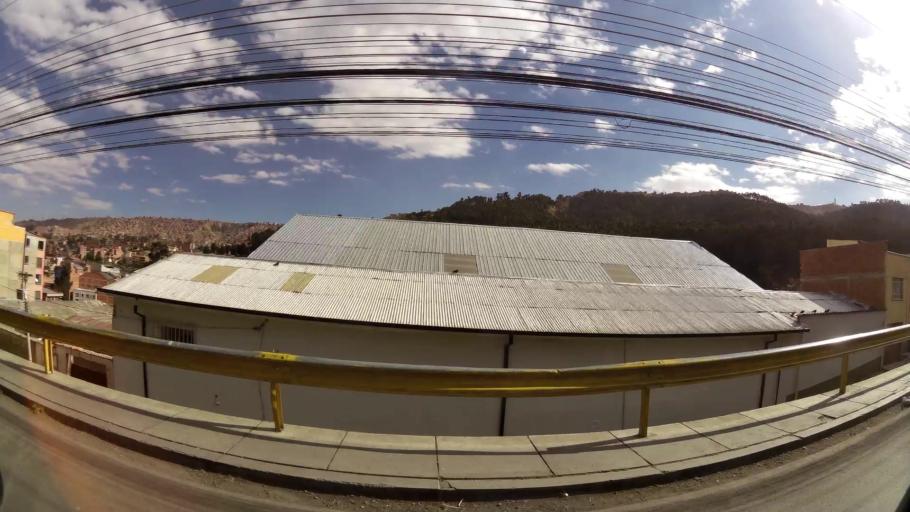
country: BO
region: La Paz
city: La Paz
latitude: -16.4792
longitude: -68.1486
